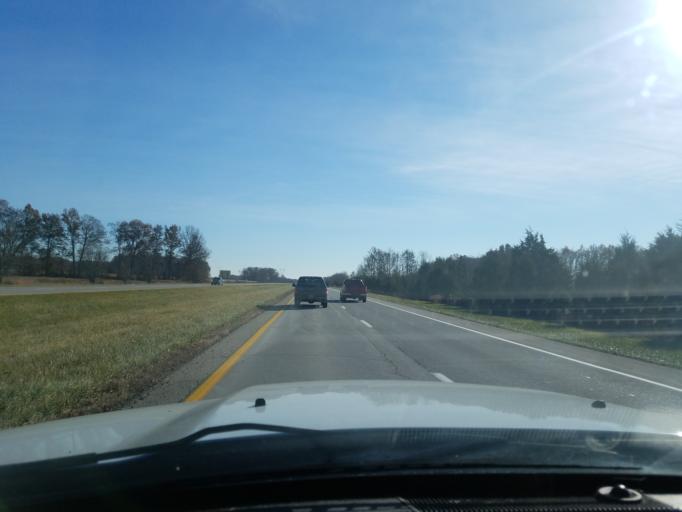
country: US
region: Ohio
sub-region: Brown County
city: Mount Orab
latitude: 39.0363
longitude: -83.9047
